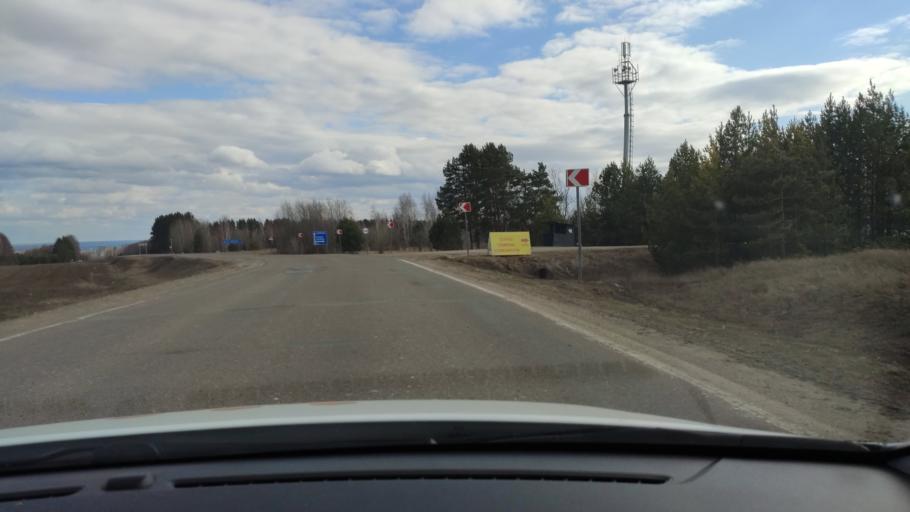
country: RU
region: Tatarstan
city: Vysokaya Gora
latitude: 56.0405
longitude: 49.2207
